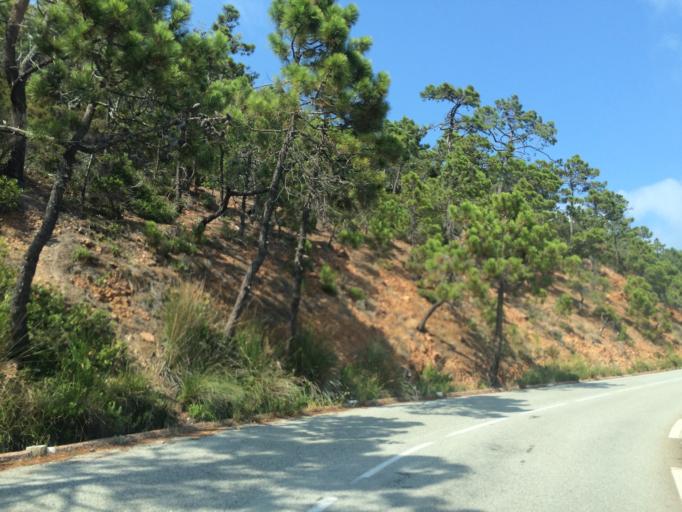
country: FR
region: Provence-Alpes-Cote d'Azur
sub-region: Departement des Alpes-Maritimes
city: Theoule-sur-Mer
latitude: 43.4473
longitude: 6.9086
